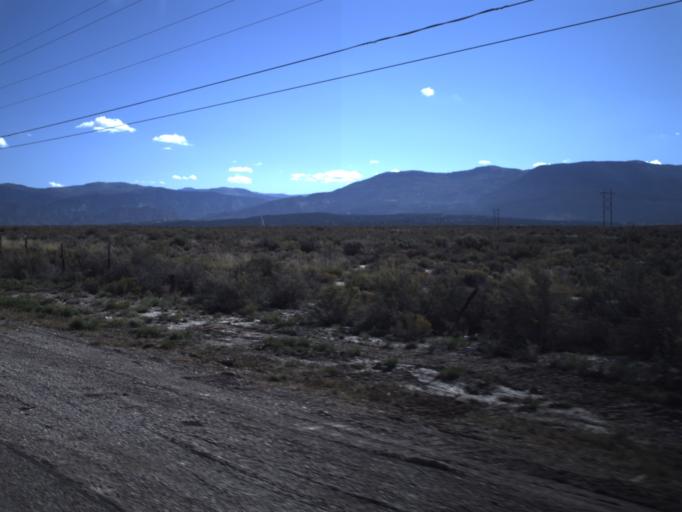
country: US
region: Utah
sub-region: Iron County
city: Cedar City
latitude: 37.6645
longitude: -113.2042
